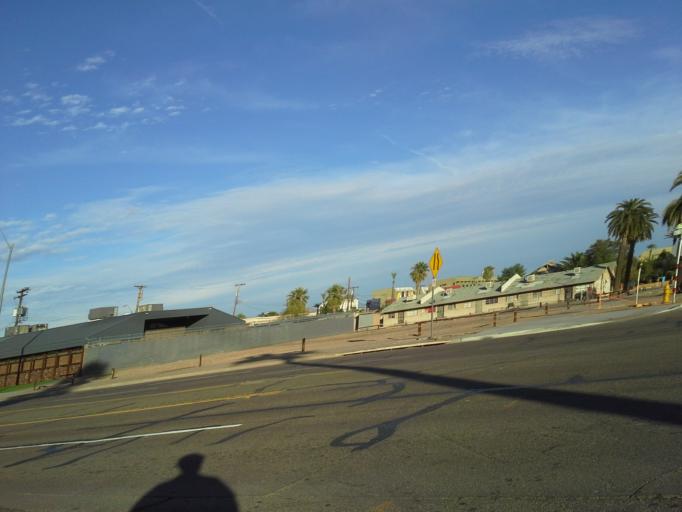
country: US
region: Arizona
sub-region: Maricopa County
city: Phoenix
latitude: 33.4600
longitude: -112.0695
